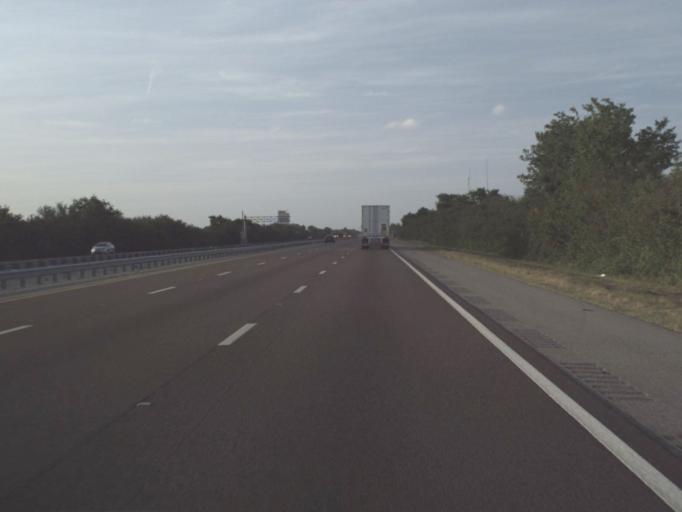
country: US
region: Florida
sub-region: Brevard County
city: Titusville
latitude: 28.5663
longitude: -80.8514
